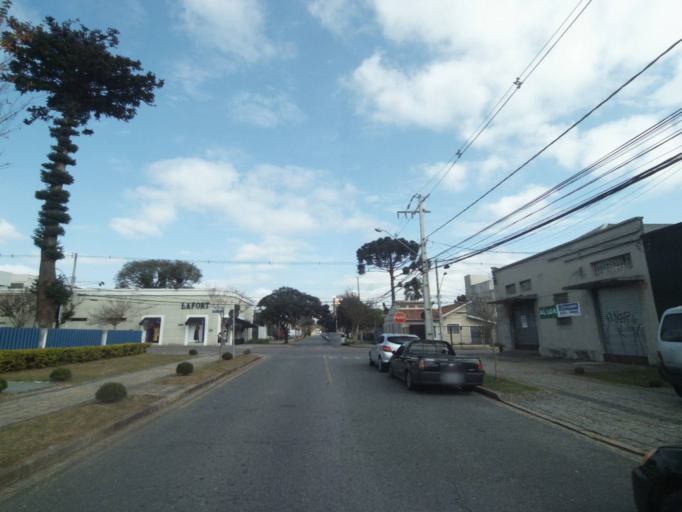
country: BR
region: Parana
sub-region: Curitiba
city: Curitiba
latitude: -25.4496
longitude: -49.2679
